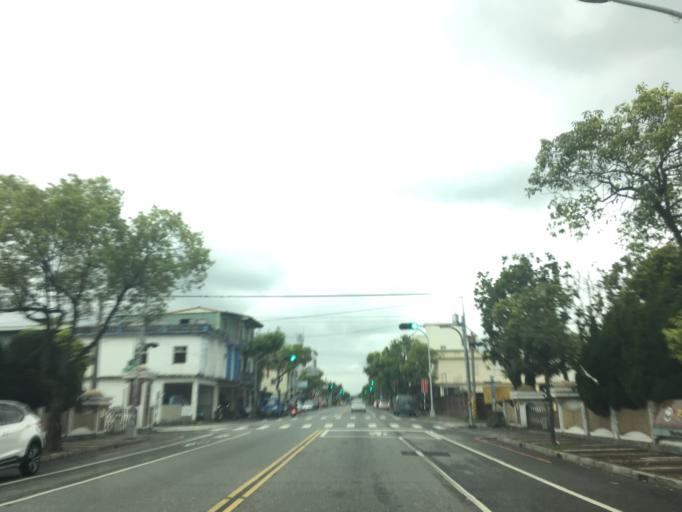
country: TW
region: Taiwan
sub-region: Hualien
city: Hualian
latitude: 23.9749
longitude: 121.5642
